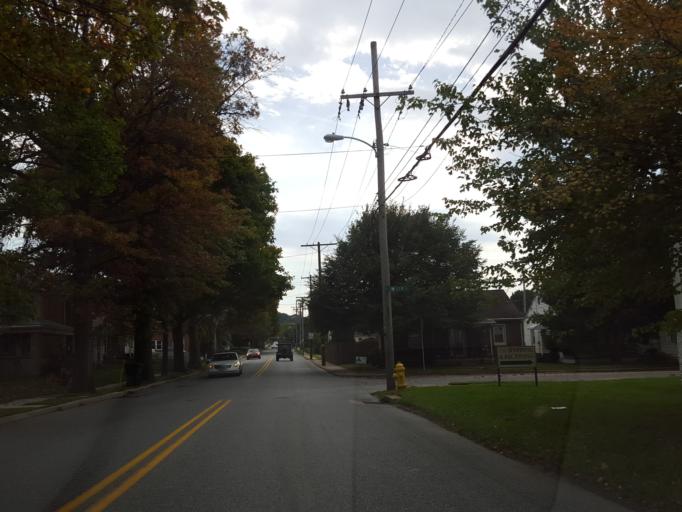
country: US
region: Pennsylvania
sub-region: York County
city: Valley View
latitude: 39.9630
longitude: -76.6996
